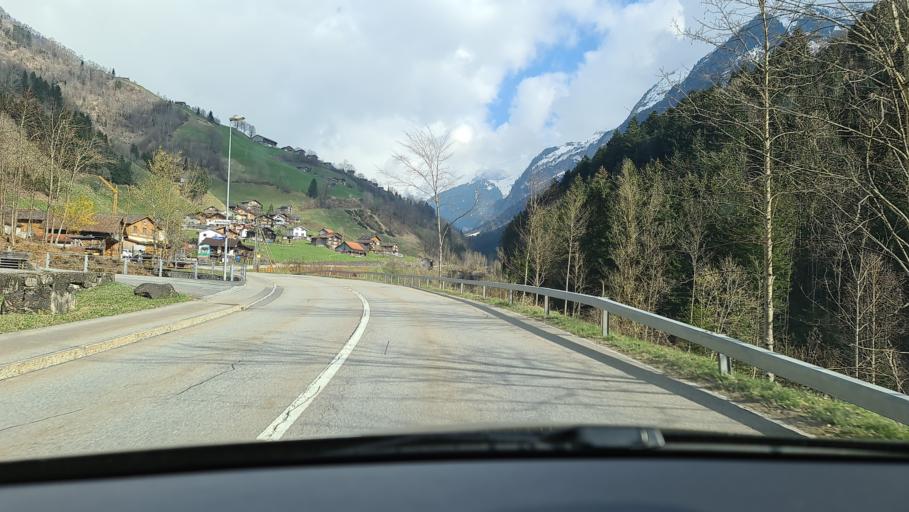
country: CH
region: Uri
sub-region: Uri
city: Burglen
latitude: 46.8765
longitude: 8.7102
